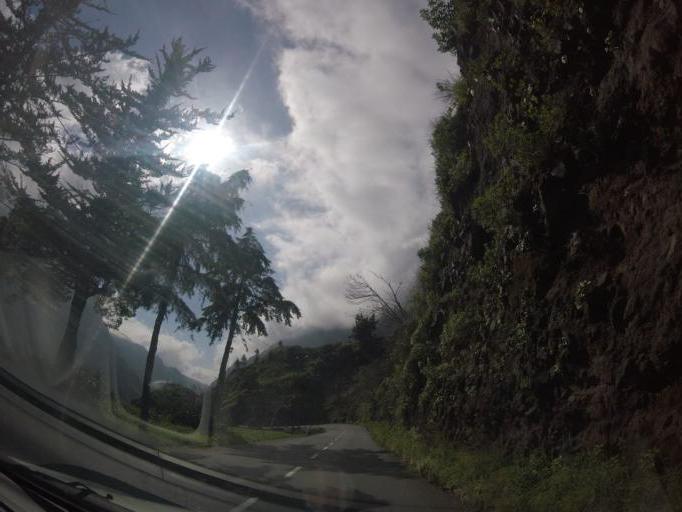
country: PT
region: Madeira
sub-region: Camara de Lobos
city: Curral das Freiras
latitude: 32.7333
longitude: -17.0233
